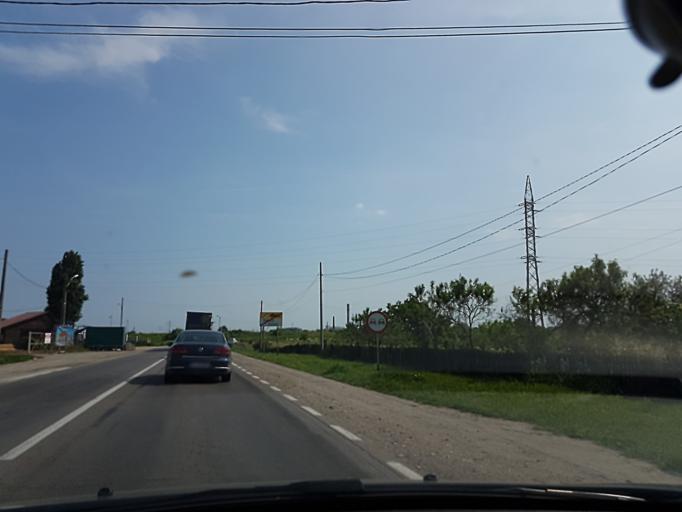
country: RO
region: Prahova
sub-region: Comuna Blejoiu
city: Blejoi
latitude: 44.9998
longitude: 26.0184
